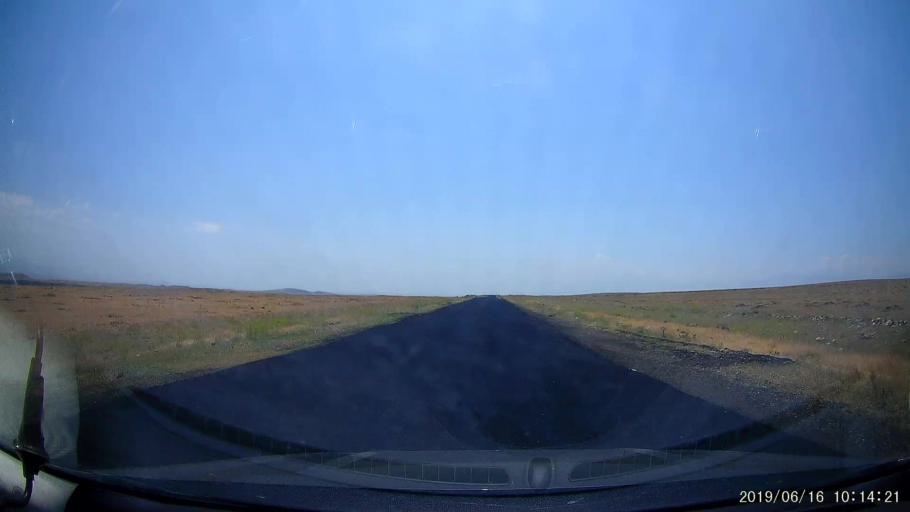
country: TR
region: Igdir
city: Tuzluca
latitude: 40.1857
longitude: 43.6608
